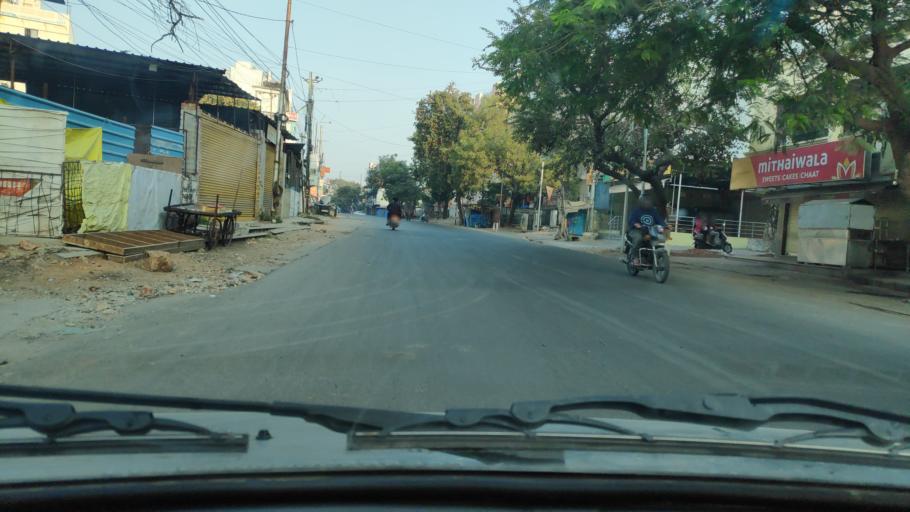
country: IN
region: Telangana
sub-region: Rangareddi
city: Gaddi Annaram
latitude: 17.3672
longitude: 78.5203
